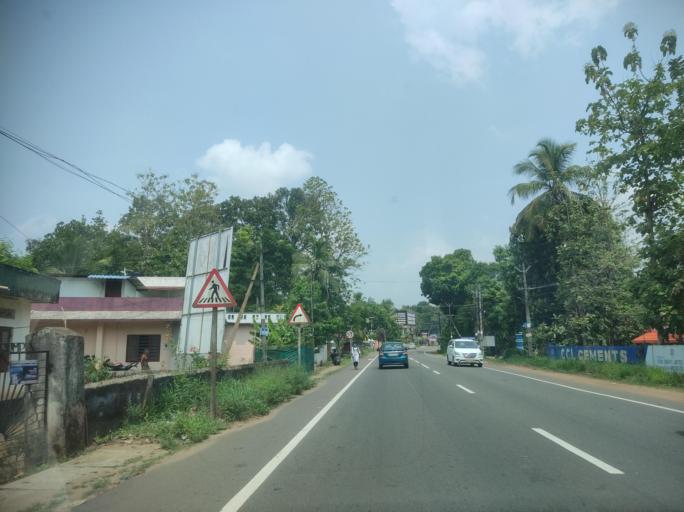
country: IN
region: Kerala
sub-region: Pattanamtitta
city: Tiruvalla
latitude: 9.4096
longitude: 76.5561
